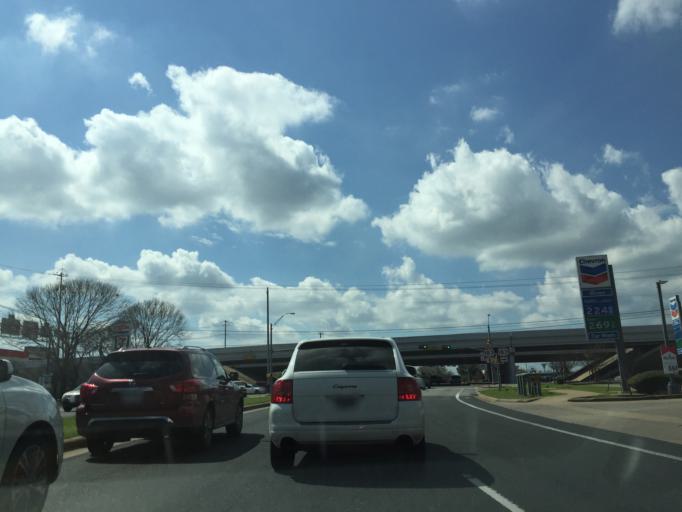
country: US
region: Texas
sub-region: Williamson County
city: Anderson Mill
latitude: 30.4618
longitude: -97.7927
